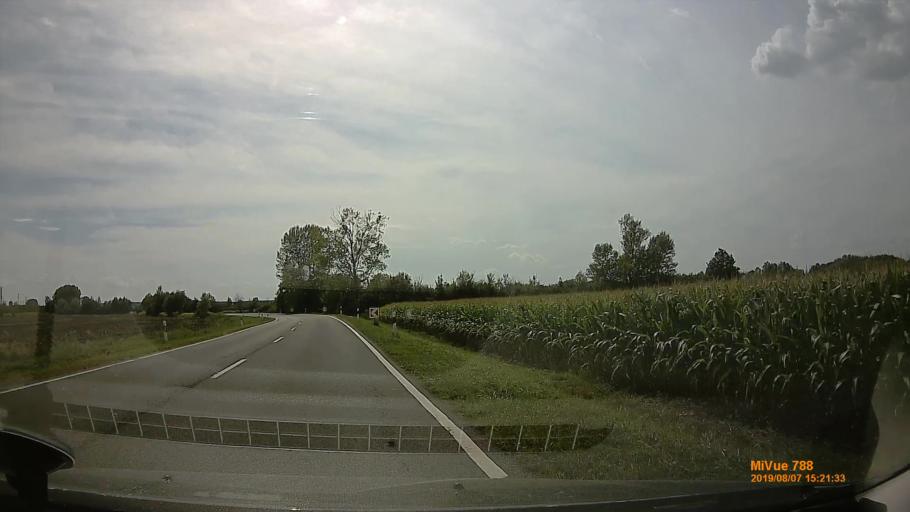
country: HU
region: Vas
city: Sarvar
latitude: 47.3367
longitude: 16.8629
